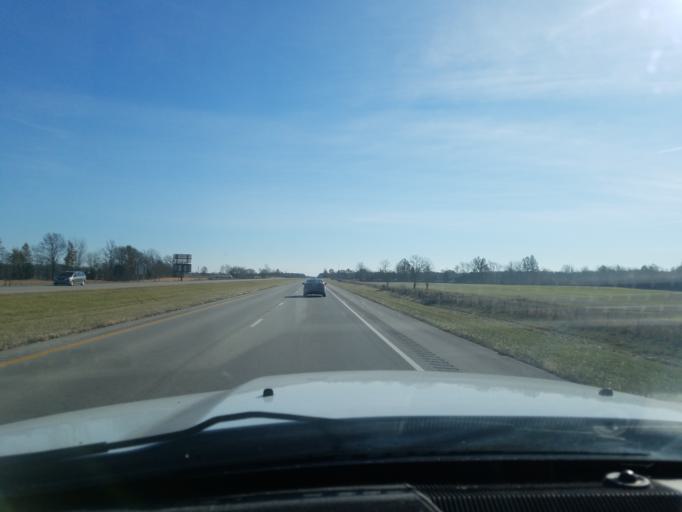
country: US
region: Ohio
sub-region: Adams County
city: Winchester
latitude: 38.9641
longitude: -83.7203
